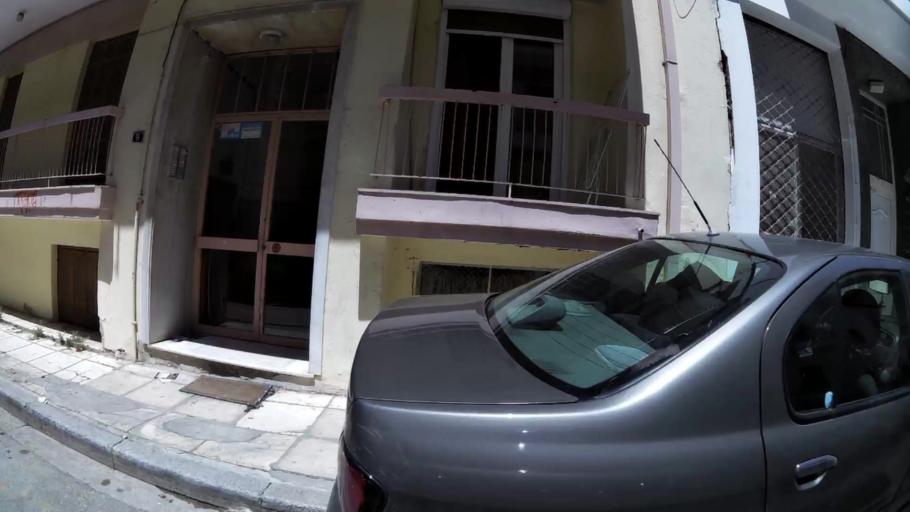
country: GR
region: Central Macedonia
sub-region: Nomos Thessalonikis
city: Triandria
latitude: 40.6061
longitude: 22.9555
